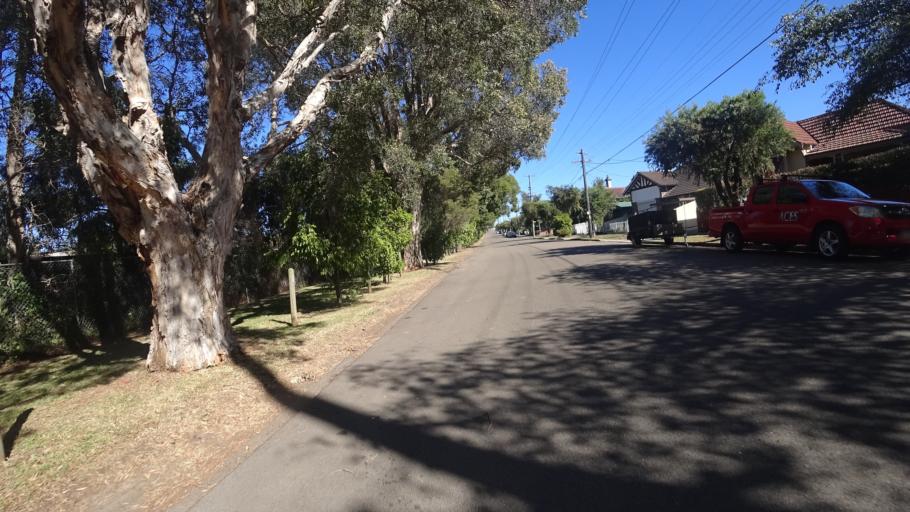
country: AU
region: New South Wales
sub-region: Kogarah
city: Kogarah Bay
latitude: -33.9686
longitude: 151.1216
